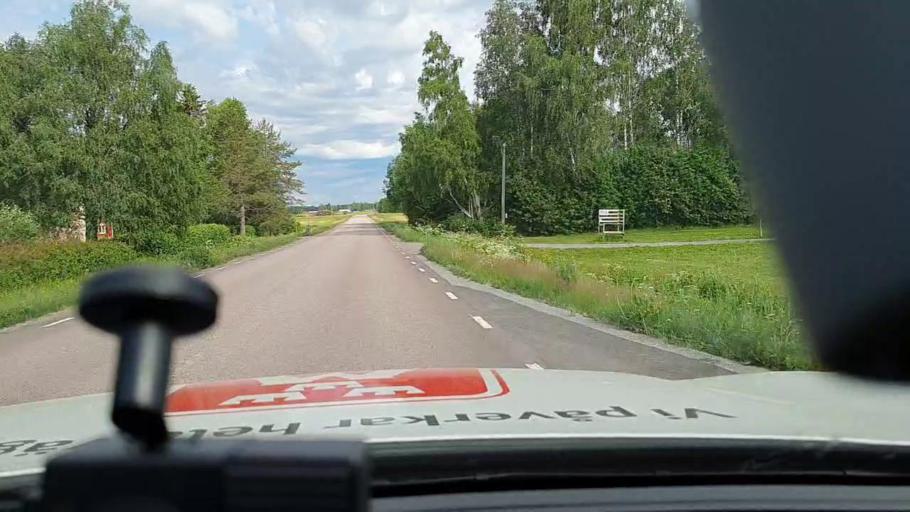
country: SE
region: Norrbotten
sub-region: Bodens Kommun
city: Saevast
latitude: 65.6966
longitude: 21.7773
